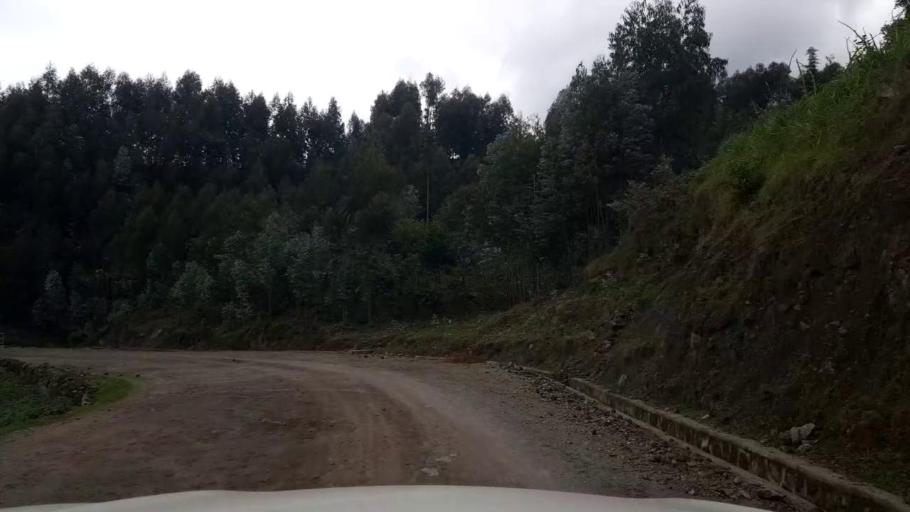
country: RW
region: Northern Province
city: Musanze
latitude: -1.5295
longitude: 29.5308
